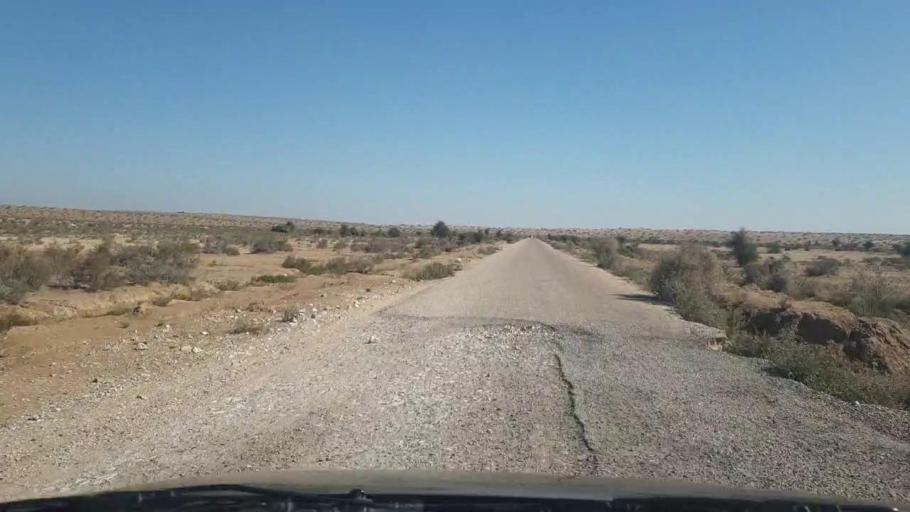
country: PK
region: Sindh
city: Bozdar
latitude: 27.0009
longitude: 68.8195
